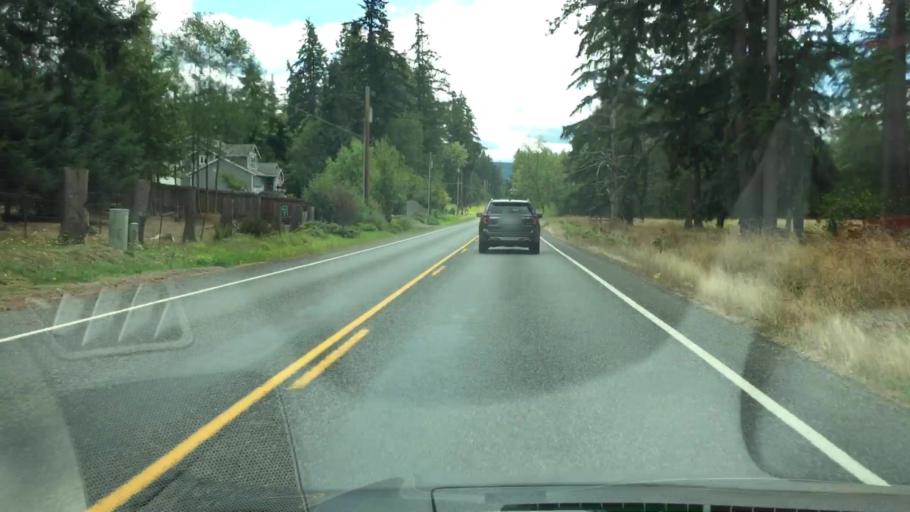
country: US
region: Washington
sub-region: Pierce County
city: Eatonville
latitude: 46.9001
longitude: -122.2977
